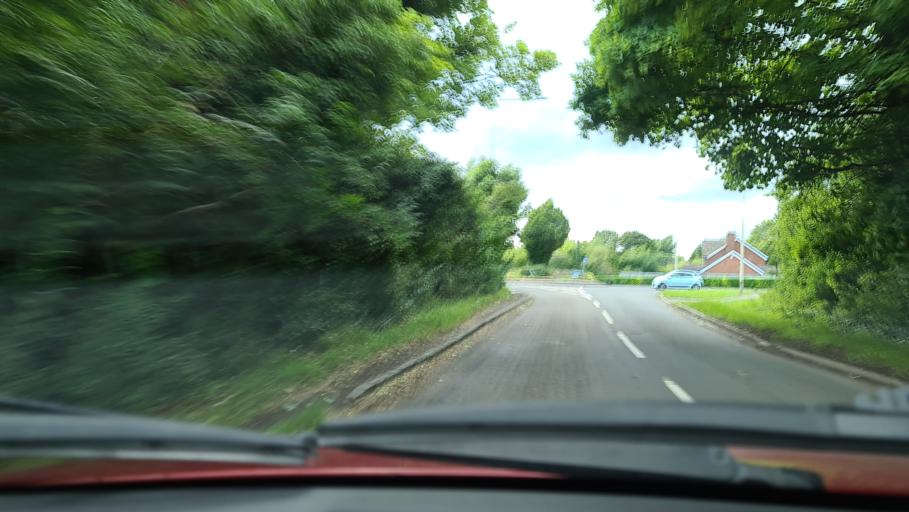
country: GB
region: England
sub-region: Buckinghamshire
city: Princes Risborough
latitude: 51.7385
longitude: -0.8149
